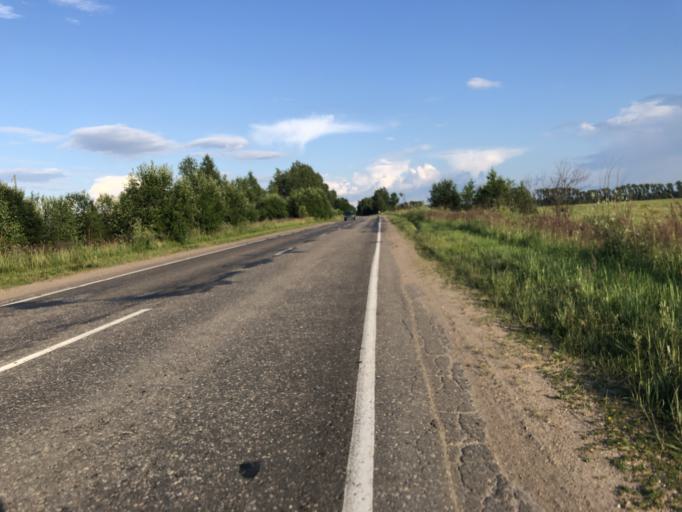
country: RU
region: Tverskaya
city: Rzhev
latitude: 56.2773
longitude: 34.2373
